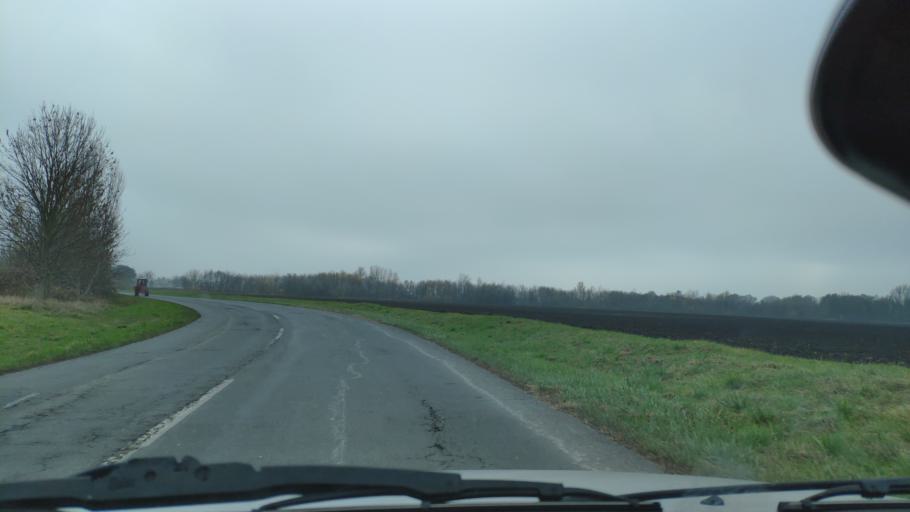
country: HU
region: Somogy
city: Balatonbereny
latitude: 46.6839
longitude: 17.2823
